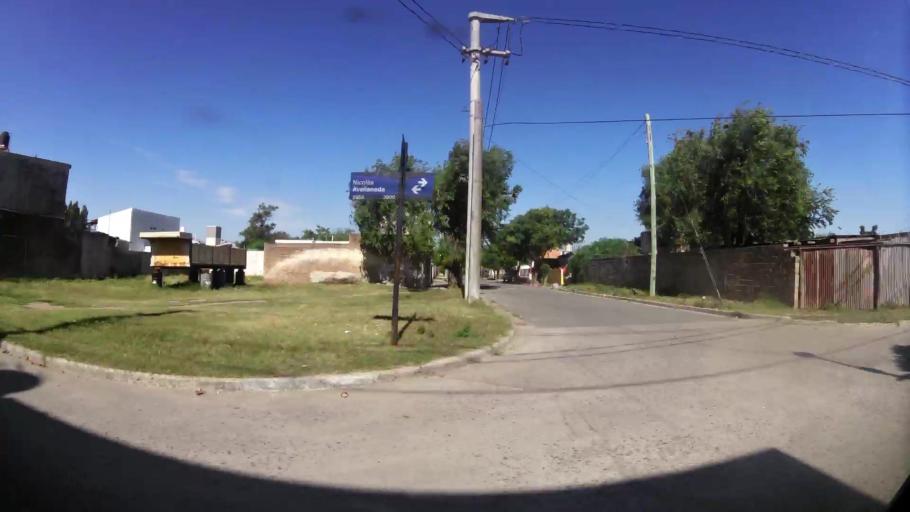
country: AR
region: Cordoba
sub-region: Departamento de Capital
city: Cordoba
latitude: -31.3744
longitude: -64.1836
